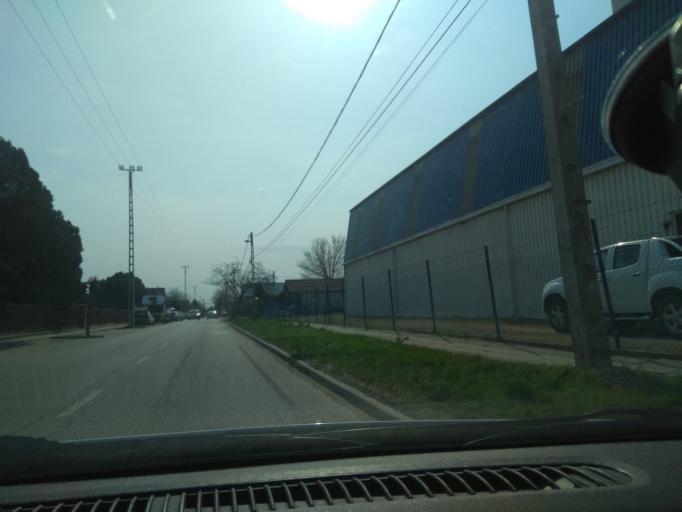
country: HU
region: Pest
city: Szigetszentmiklos
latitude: 47.3551
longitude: 19.0489
